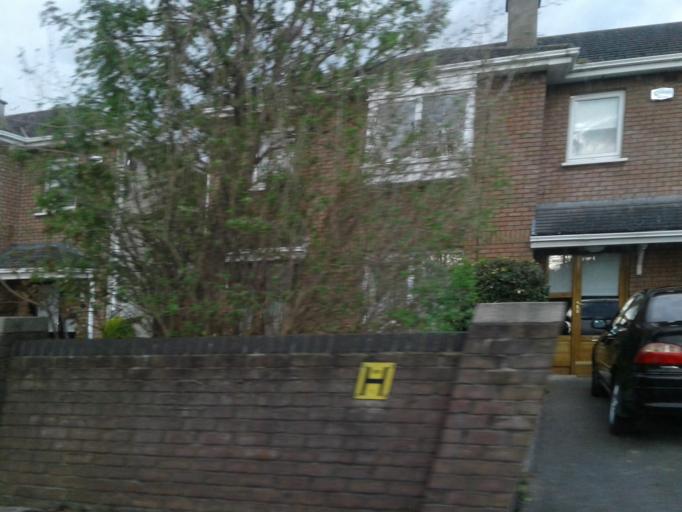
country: IE
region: Leinster
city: Beaumont
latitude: 53.3915
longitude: -6.2282
